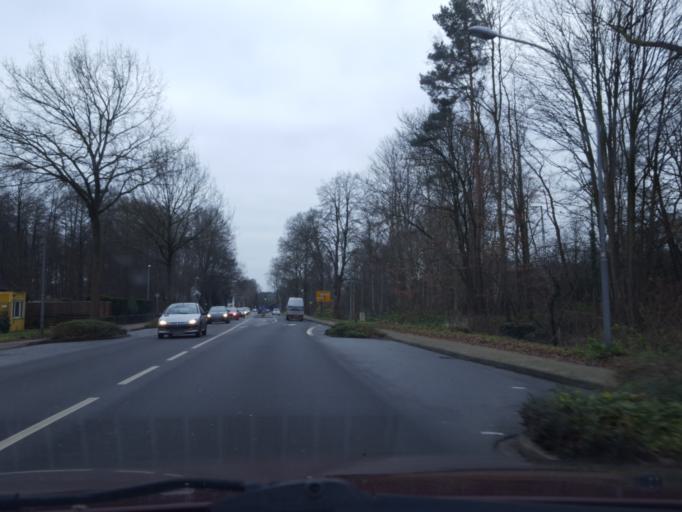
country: DE
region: Lower Saxony
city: Verden
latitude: 52.9440
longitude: 9.2327
